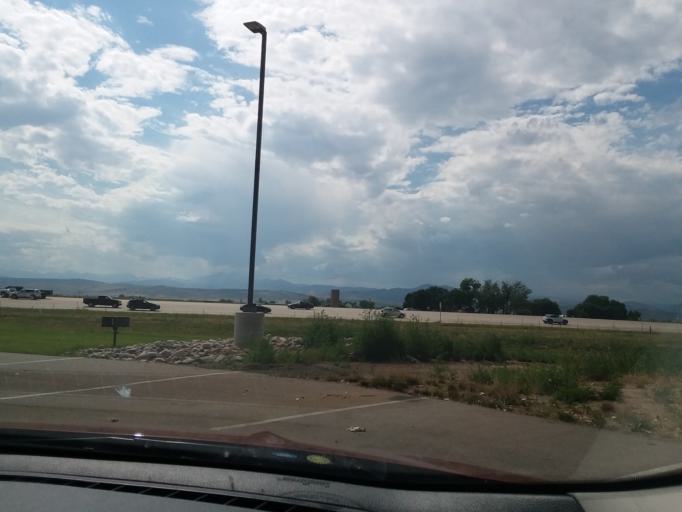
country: US
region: Colorado
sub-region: Larimer County
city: Berthoud
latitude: 40.3039
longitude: -105.1048
